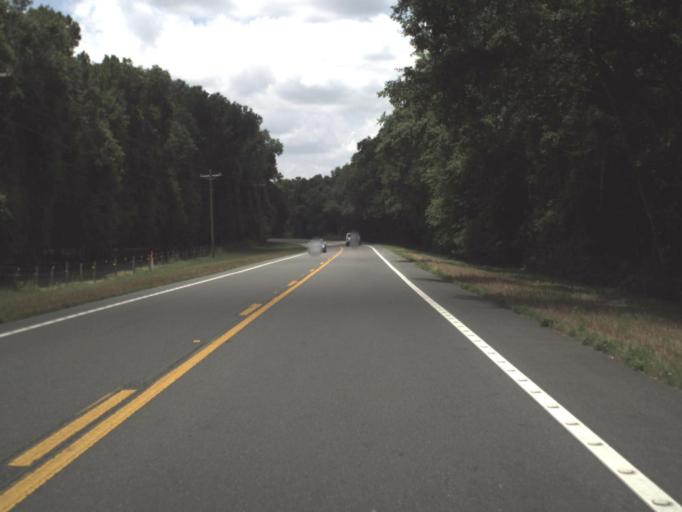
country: US
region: Florida
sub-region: Alachua County
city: Gainesville
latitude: 29.5517
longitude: -82.3928
